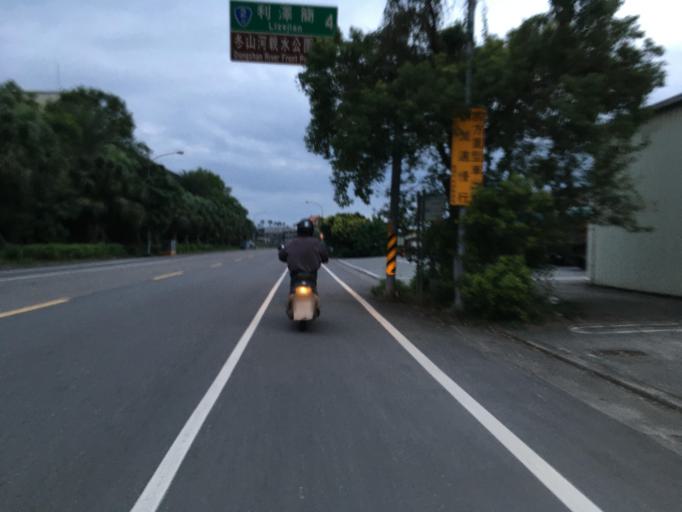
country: TW
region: Taiwan
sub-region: Yilan
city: Yilan
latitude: 24.6358
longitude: 121.8321
